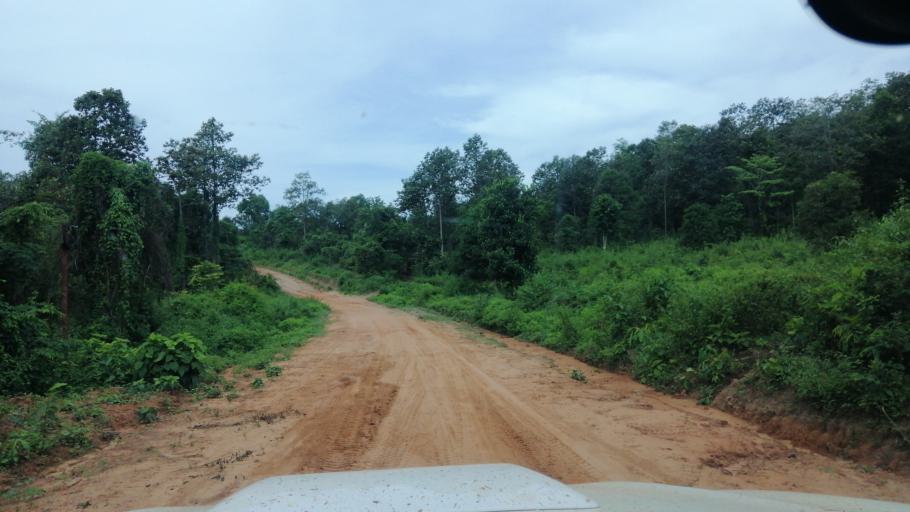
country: TH
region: Loei
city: Na Haeo
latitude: 17.5774
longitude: 101.1655
